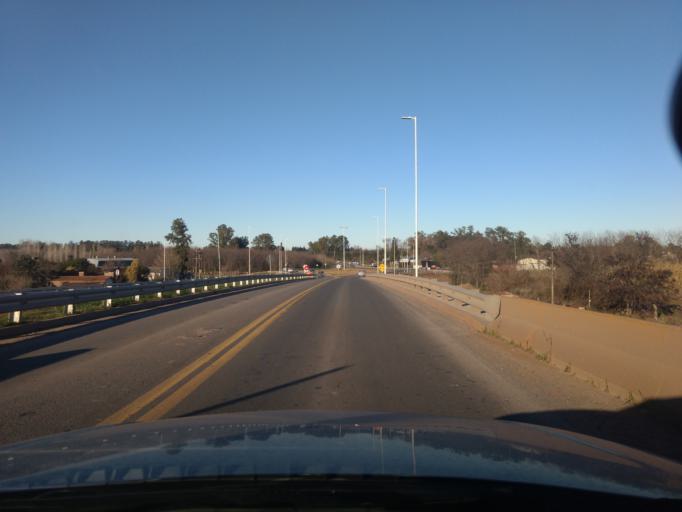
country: AR
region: Buenos Aires
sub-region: Partido de Lujan
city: Lujan
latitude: -34.5904
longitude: -59.1042
